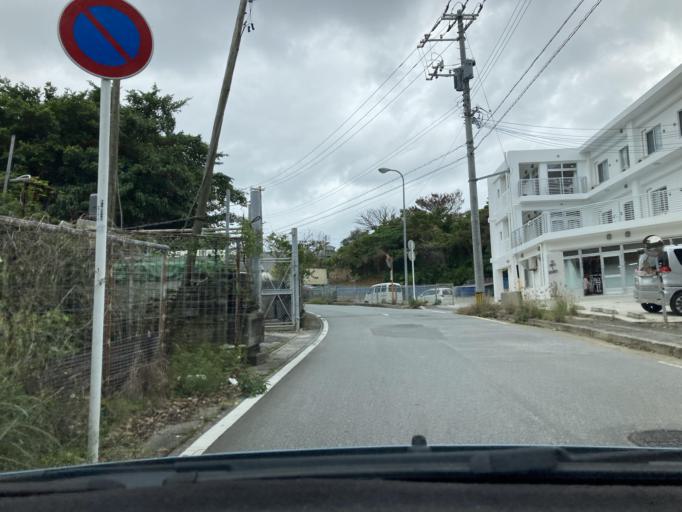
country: JP
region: Okinawa
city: Okinawa
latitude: 26.3465
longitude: 127.8068
